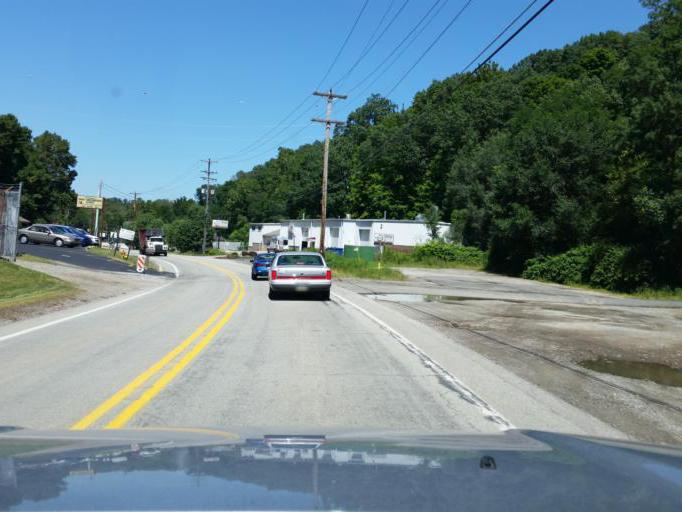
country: US
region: Pennsylvania
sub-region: Allegheny County
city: Blawnox
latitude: 40.4827
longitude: -79.8514
